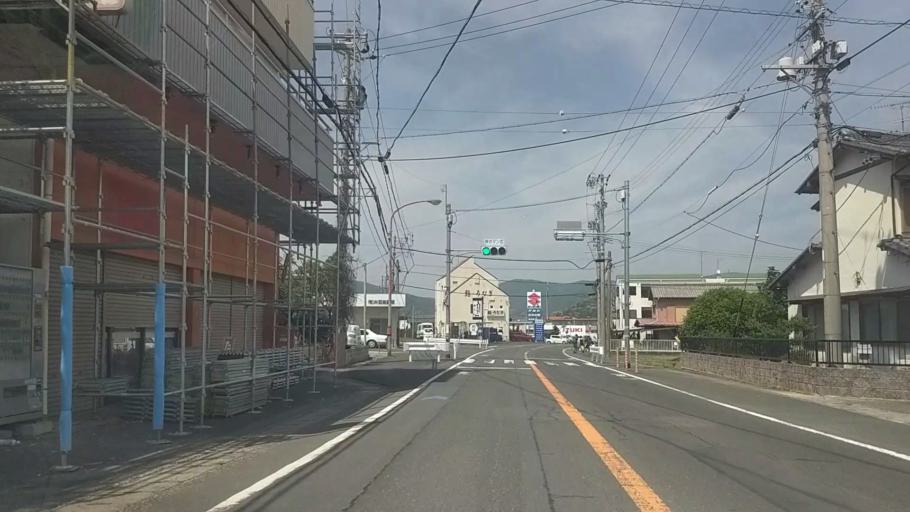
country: JP
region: Shizuoka
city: Kosai-shi
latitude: 34.7929
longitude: 137.5461
